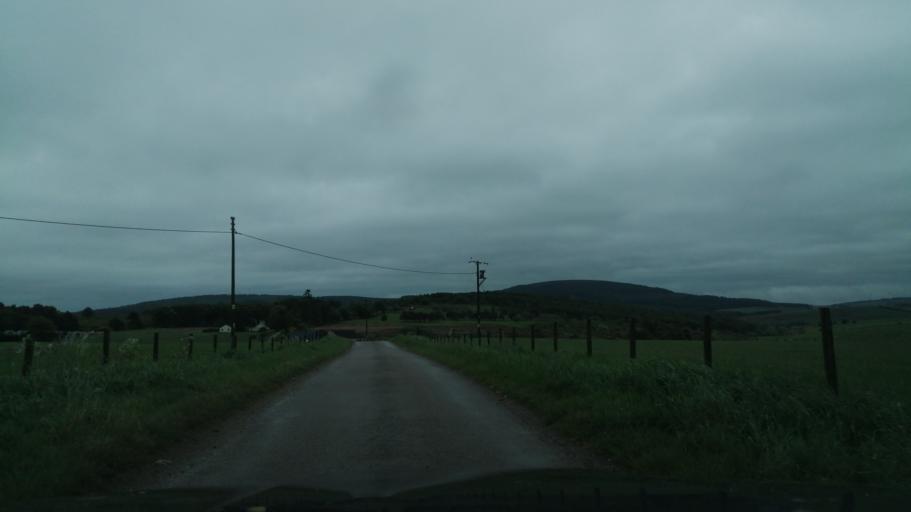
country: GB
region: Scotland
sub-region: Moray
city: Keith
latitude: 57.5714
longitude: -2.8614
